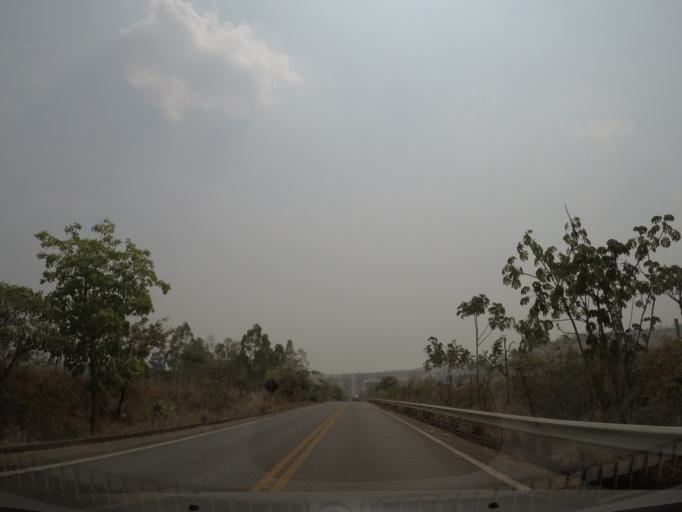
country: BR
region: Goias
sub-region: Pirenopolis
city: Pirenopolis
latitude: -15.8994
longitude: -48.8713
